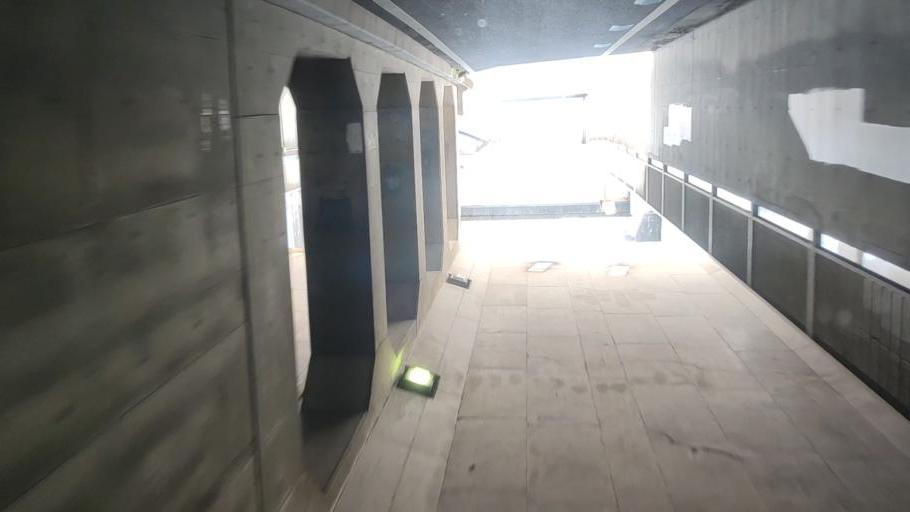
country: JP
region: Kanagawa
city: Hiratsuka
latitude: 35.3250
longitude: 139.3378
